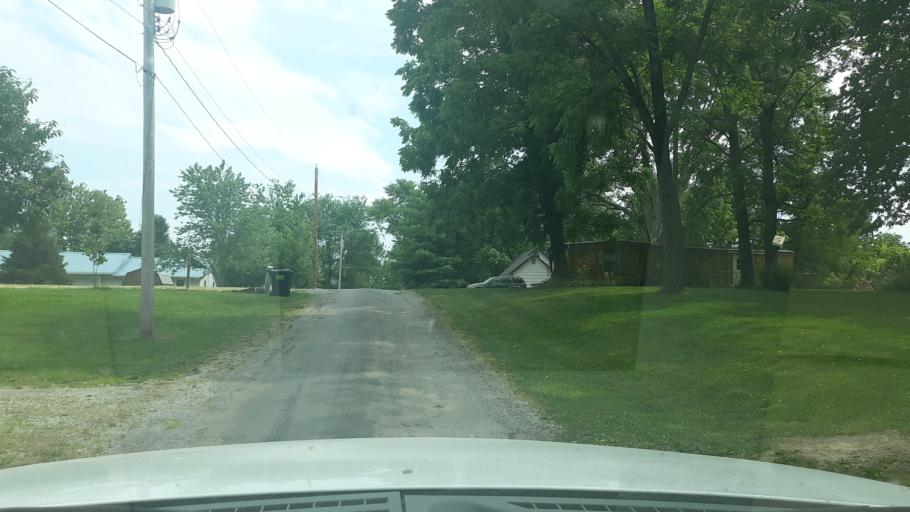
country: US
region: Illinois
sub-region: Saline County
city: Harrisburg
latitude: 37.8440
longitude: -88.6116
